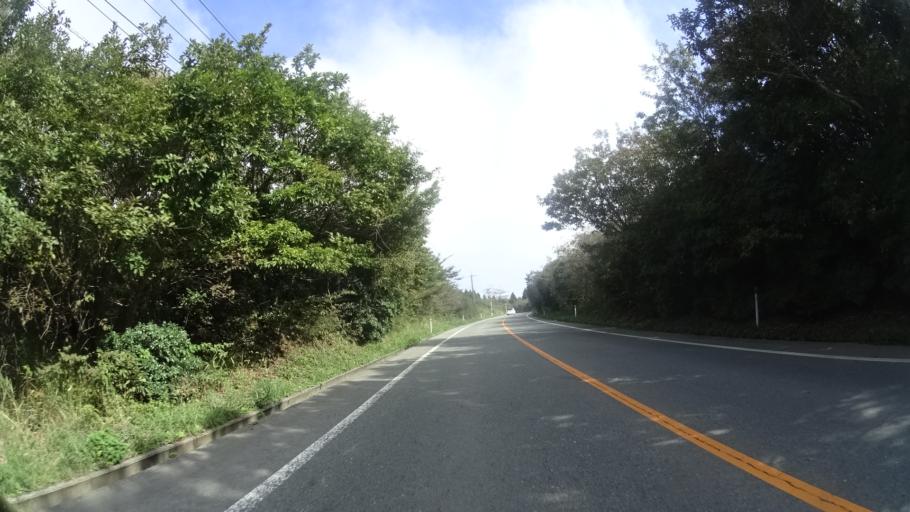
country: JP
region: Kumamoto
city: Aso
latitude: 32.9514
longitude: 130.9822
